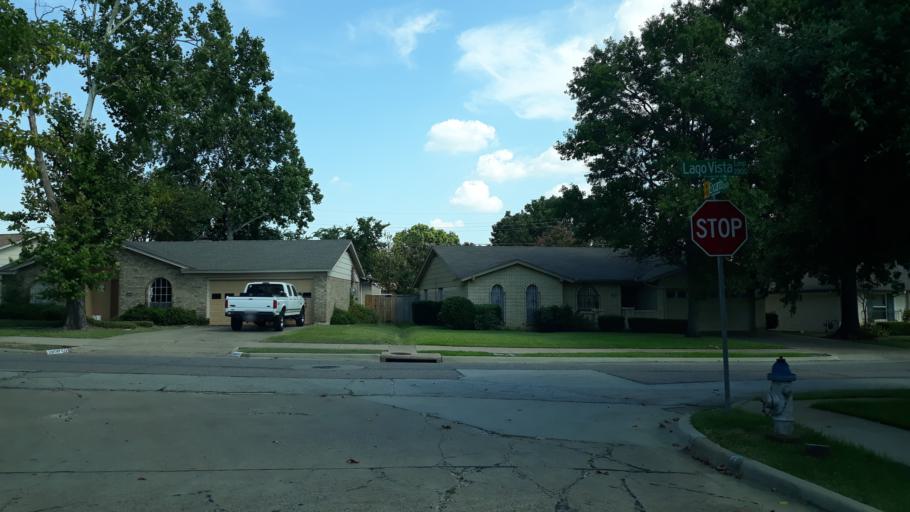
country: US
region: Texas
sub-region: Dallas County
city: Irving
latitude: 32.8464
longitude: -96.9987
